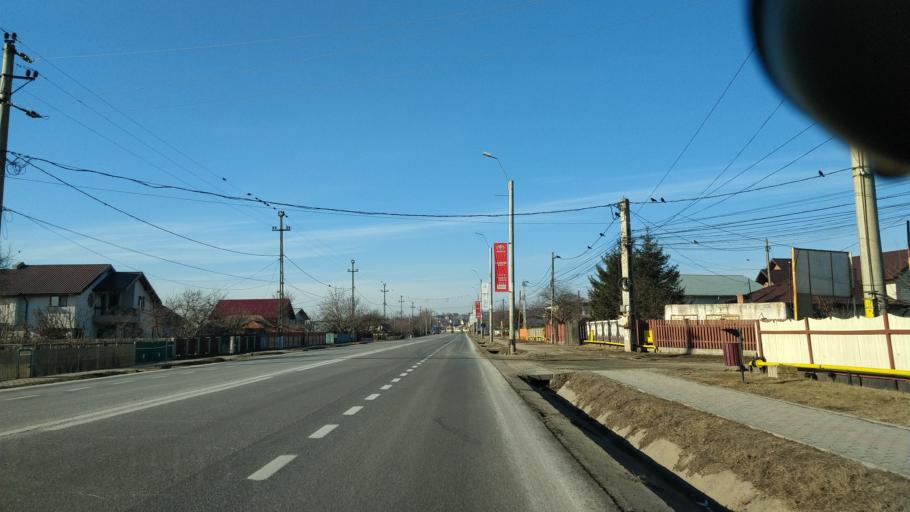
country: RO
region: Iasi
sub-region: Comuna Letcani
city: Letcani
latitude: 47.1930
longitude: 27.4224
